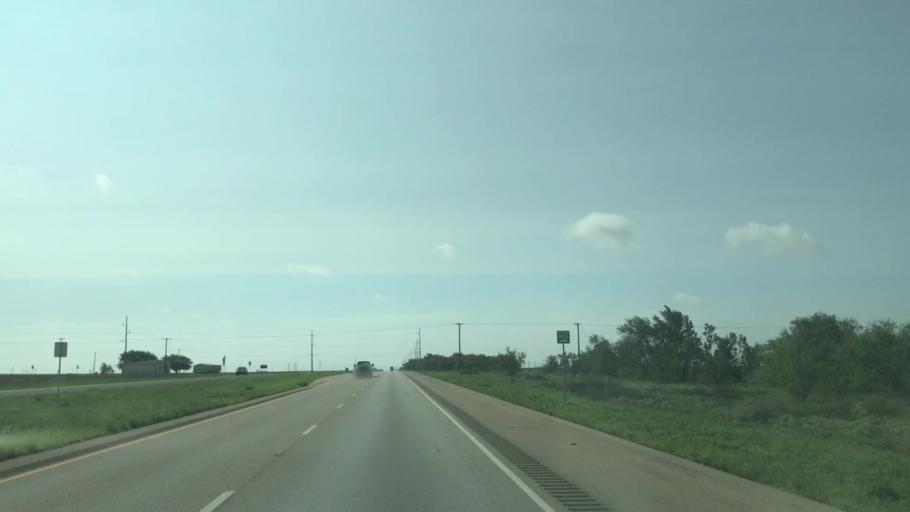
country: US
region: Texas
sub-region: Nolan County
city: Roscoe
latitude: 32.5638
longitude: -100.7086
